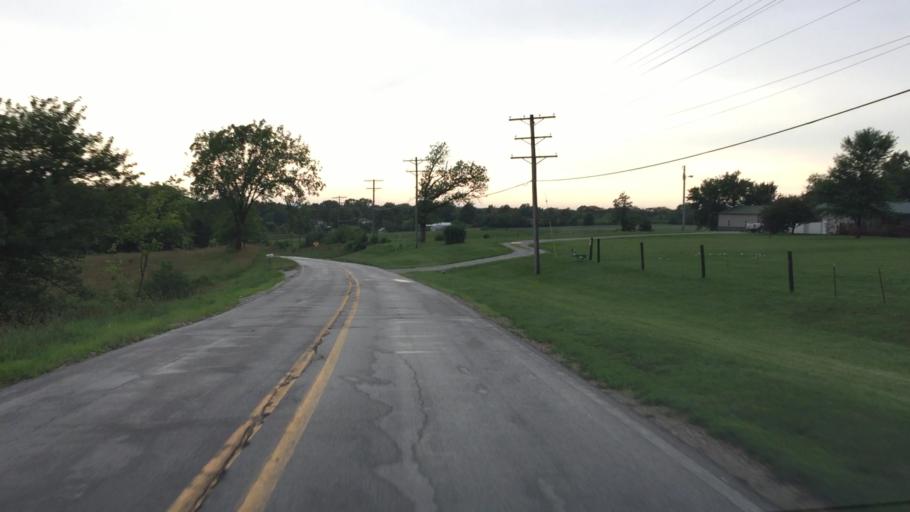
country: US
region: Illinois
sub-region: Hancock County
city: Warsaw
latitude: 40.3561
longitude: -91.4106
